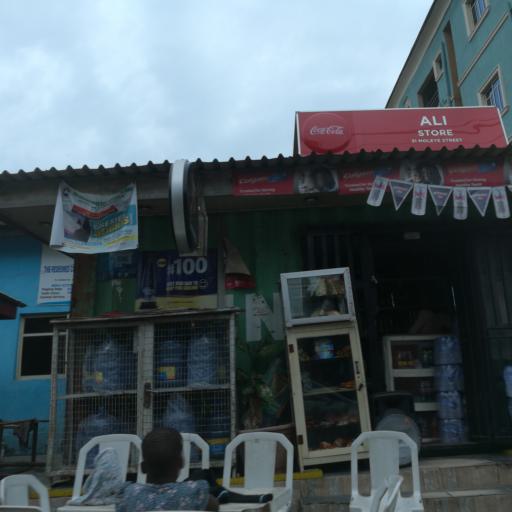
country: NG
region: Lagos
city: Makoko
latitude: 6.5007
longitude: 3.3786
